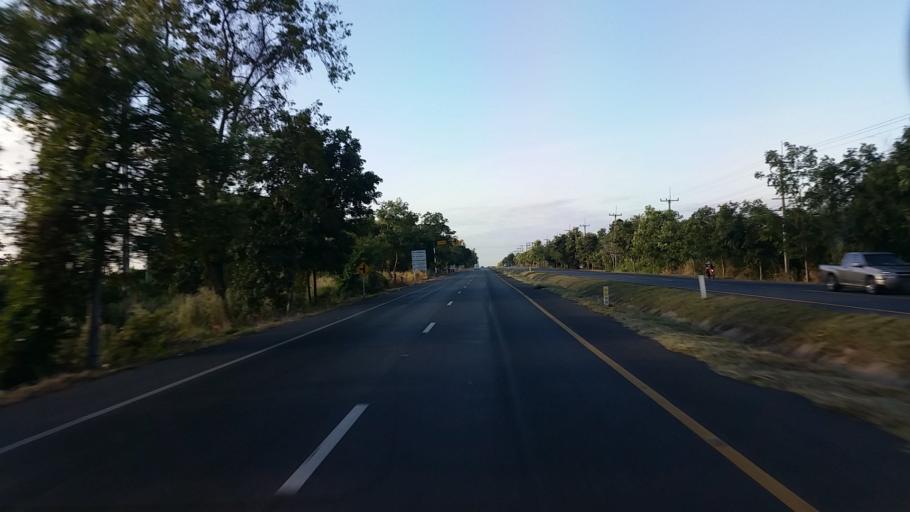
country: TH
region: Lop Buri
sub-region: Amphoe Tha Luang
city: Tha Luang
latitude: 15.1408
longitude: 101.0461
